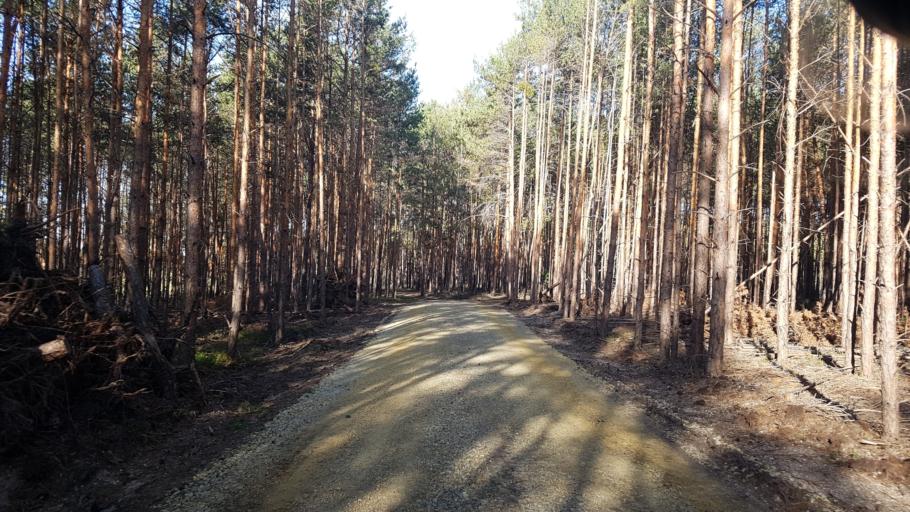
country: DE
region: Brandenburg
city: Finsterwalde
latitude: 51.5791
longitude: 13.6895
